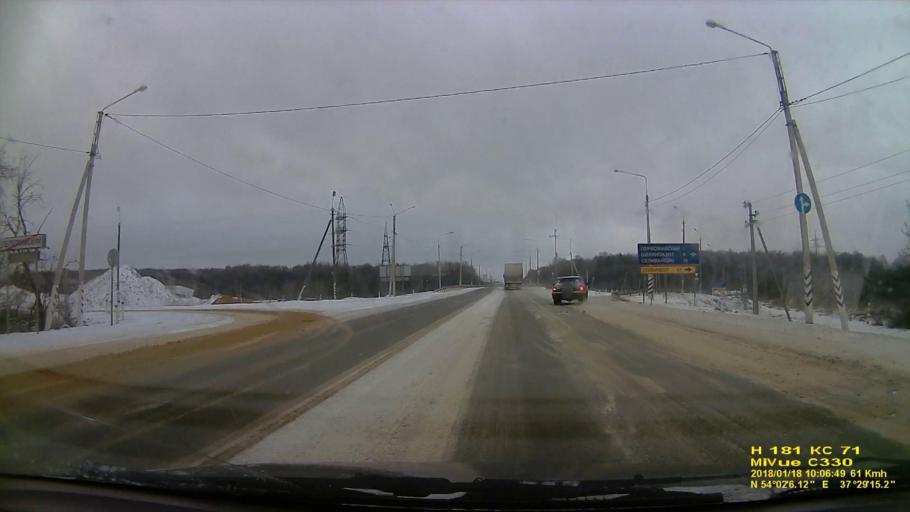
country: RU
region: Tula
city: Pervomayskiy
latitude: 54.0347
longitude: 37.4876
